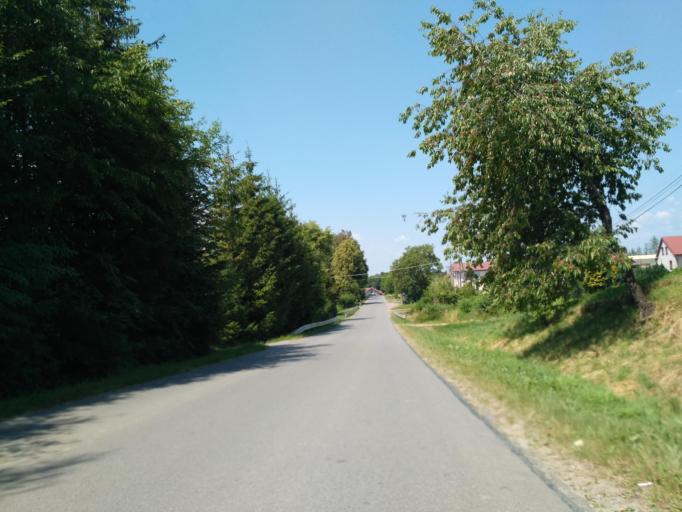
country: PL
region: Subcarpathian Voivodeship
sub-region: Powiat sanocki
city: Niebieszczany
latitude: 49.5087
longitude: 22.1535
